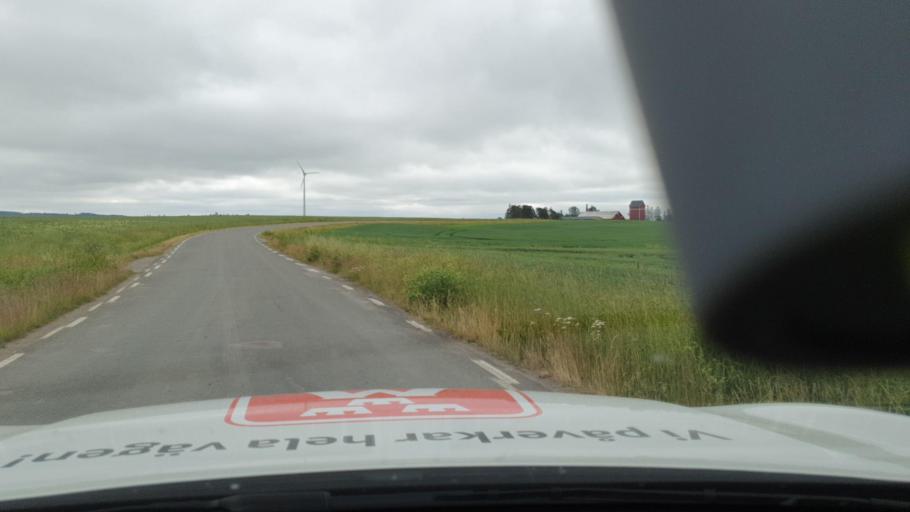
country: SE
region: Vaestra Goetaland
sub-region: Tibro Kommun
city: Tibro
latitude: 58.3796
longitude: 14.1157
